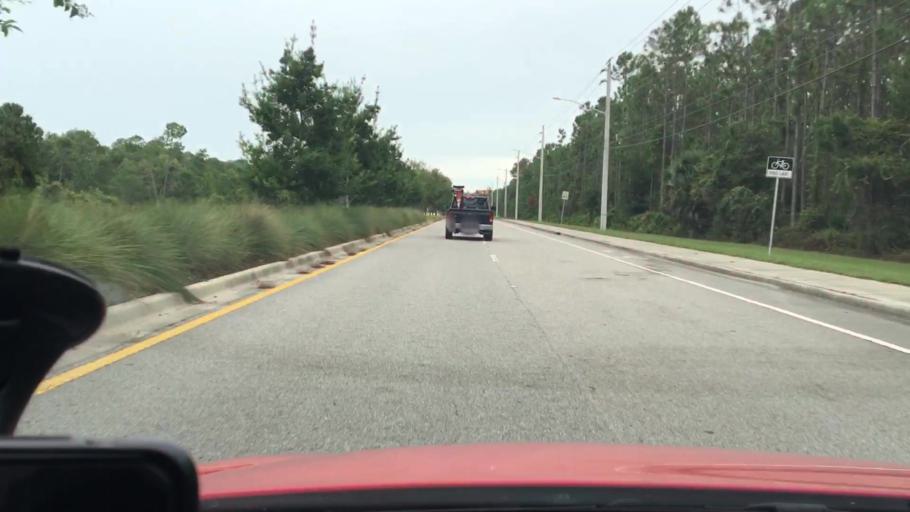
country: US
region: Florida
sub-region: Flagler County
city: Flagler Beach
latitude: 29.4953
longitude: -81.1894
